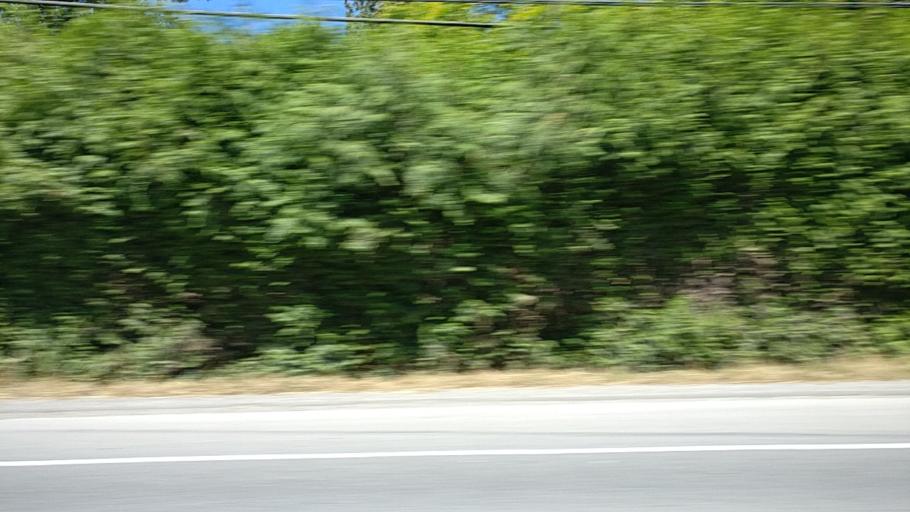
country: CA
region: British Columbia
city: Aldergrove
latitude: 49.0170
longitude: -122.4102
